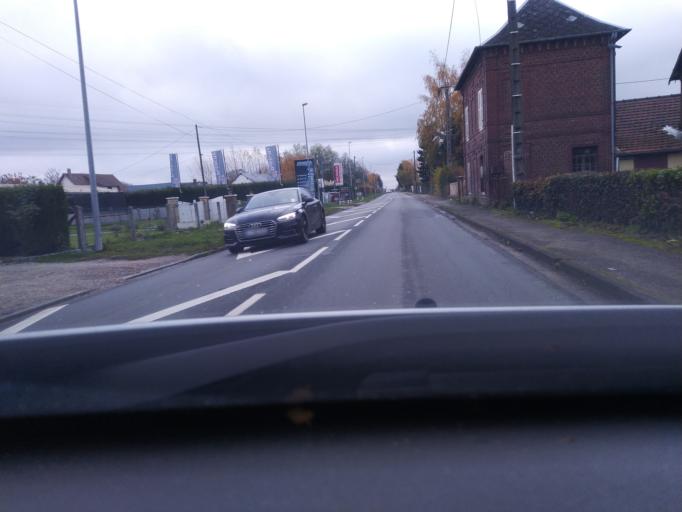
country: FR
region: Haute-Normandie
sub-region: Departement de la Seine-Maritime
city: La Vaupaliere
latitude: 49.4863
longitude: 1.0096
